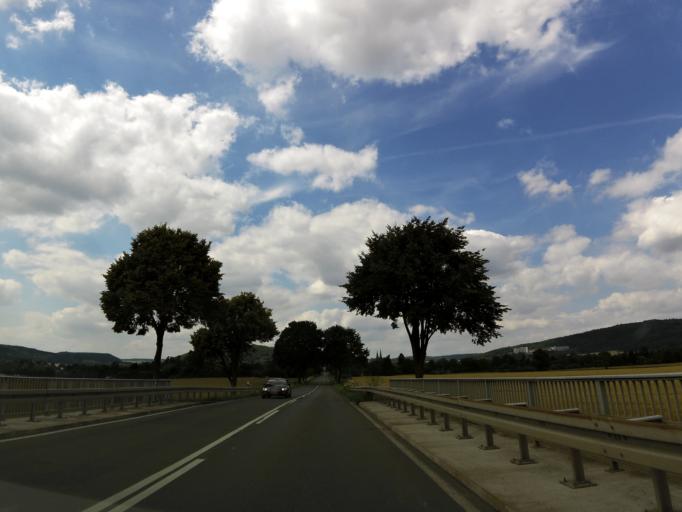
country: DE
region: North Rhine-Westphalia
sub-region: Regierungsbezirk Detmold
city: Hoexter
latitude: 51.7673
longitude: 9.3937
